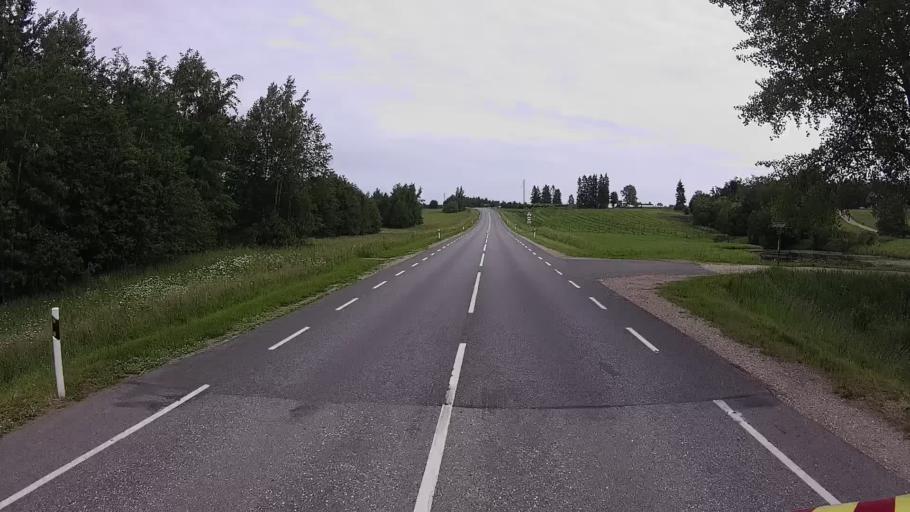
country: EE
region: Viljandimaa
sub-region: Karksi vald
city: Karksi-Nuia
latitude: 58.1476
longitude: 25.5932
